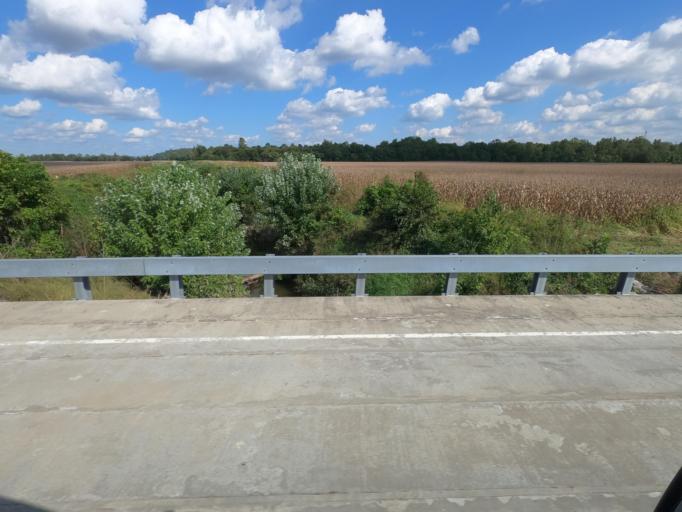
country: US
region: Illinois
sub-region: Massac County
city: Metropolis
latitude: 37.2817
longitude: -88.7577
